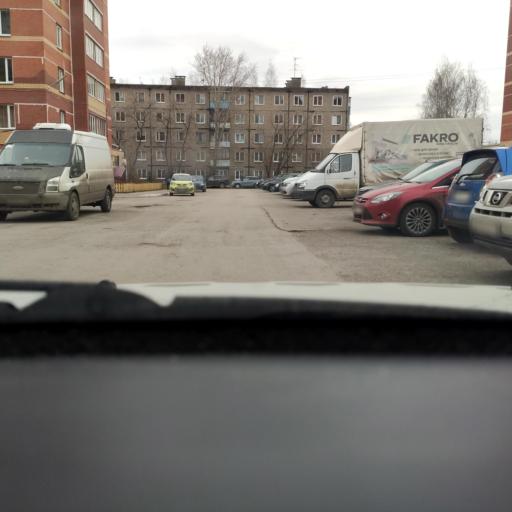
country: RU
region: Perm
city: Polazna
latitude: 58.1267
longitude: 56.3888
